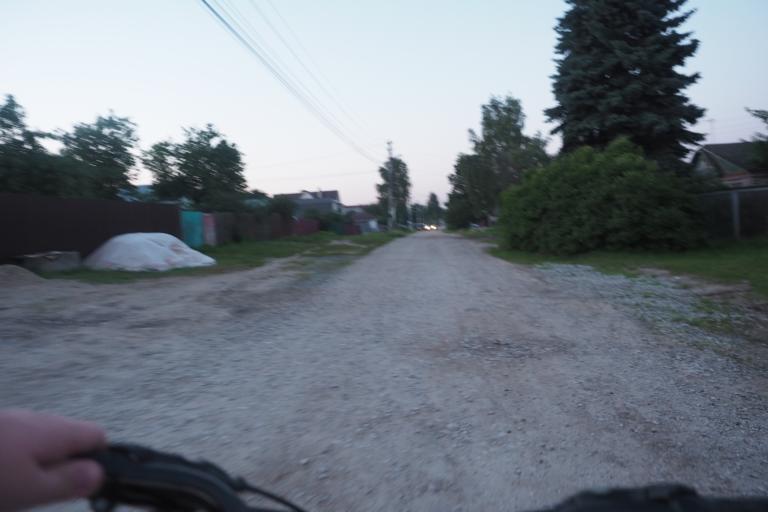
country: RU
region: Moskovskaya
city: Ramenskoye
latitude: 55.5557
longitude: 38.3056
